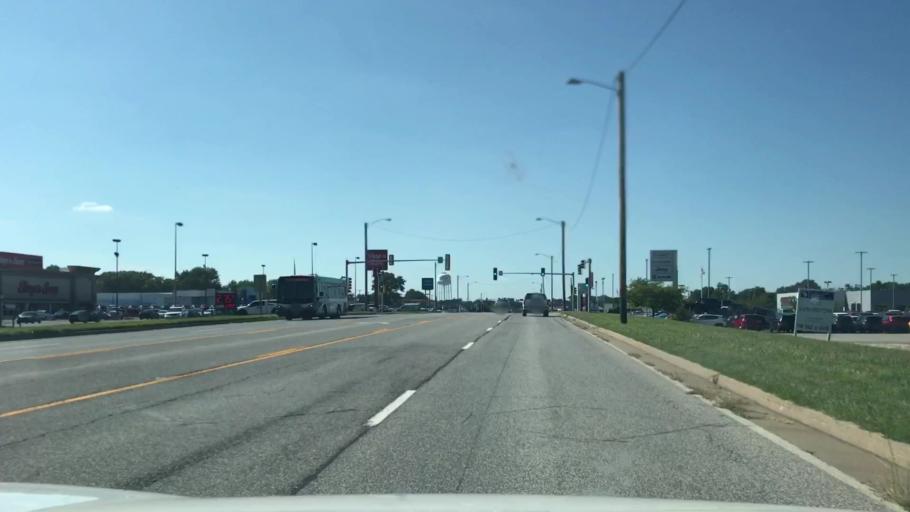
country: US
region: Illinois
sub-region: Madison County
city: Roxana
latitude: 38.8567
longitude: -90.0647
